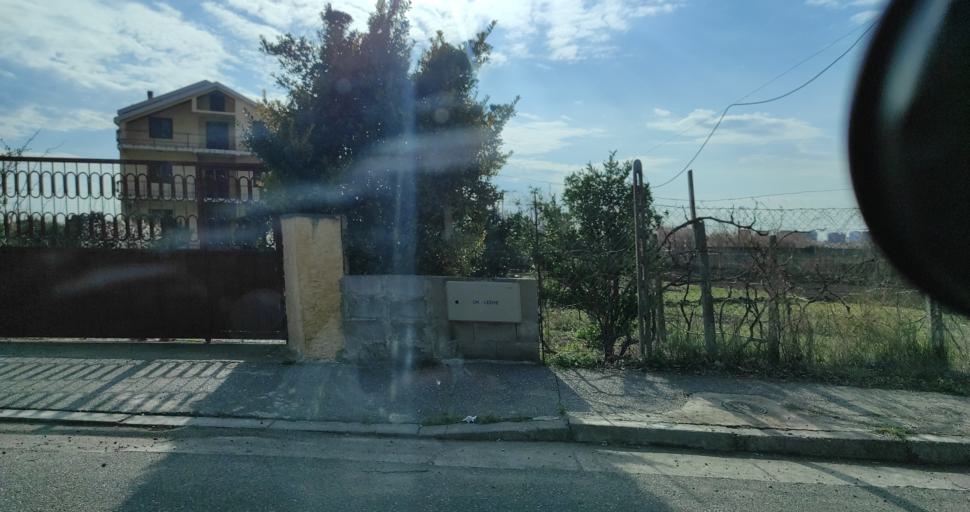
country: AL
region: Lezhe
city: Lezhe
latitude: 41.7945
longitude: 19.6211
